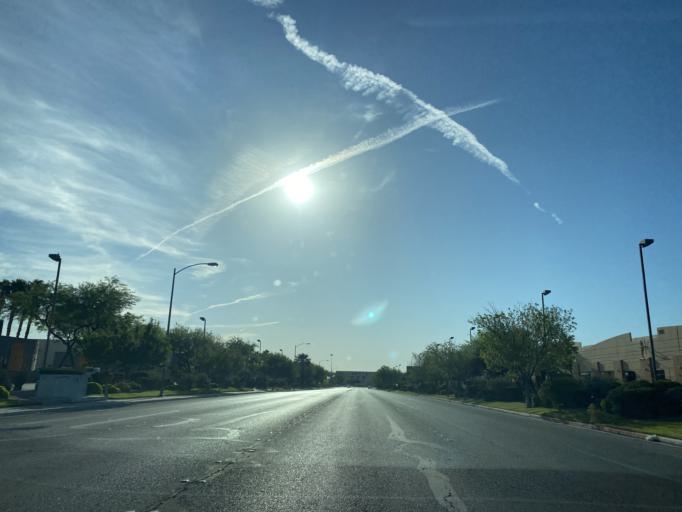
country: US
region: Nevada
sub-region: Clark County
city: Paradise
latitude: 36.0679
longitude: -115.1522
